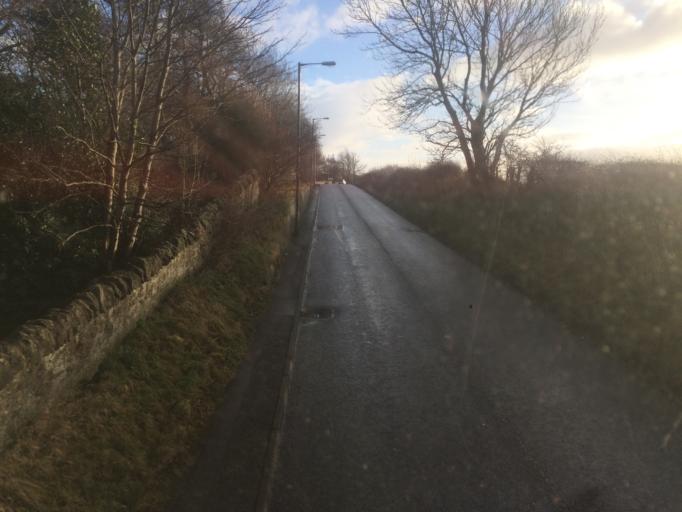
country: GB
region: Scotland
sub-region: Midlothian
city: Loanhead
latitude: 55.8674
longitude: -3.1750
